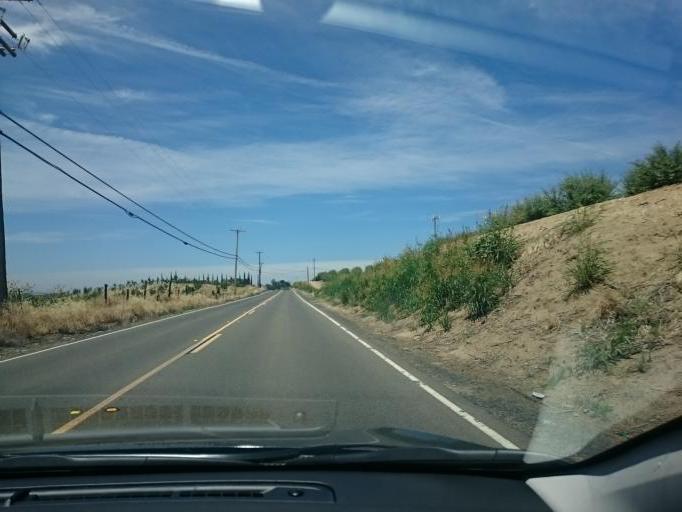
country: US
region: California
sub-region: Stanislaus County
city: Waterford
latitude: 37.6403
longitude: -120.6253
